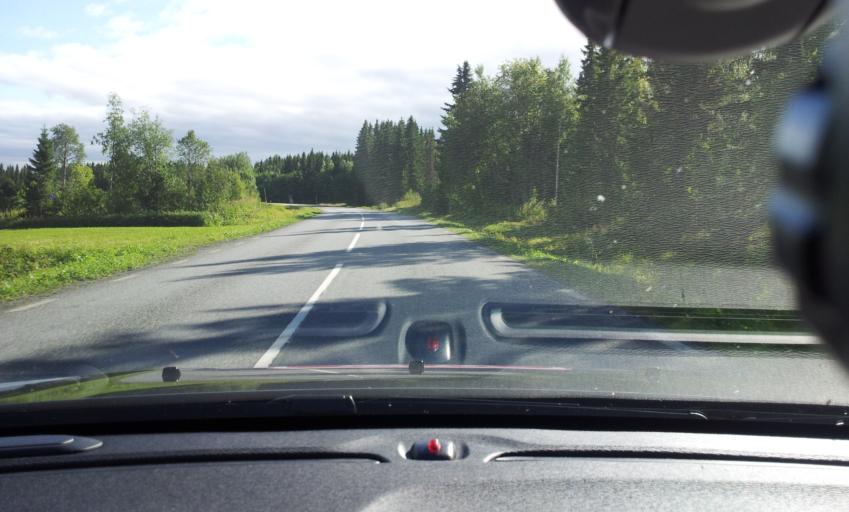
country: SE
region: Jaemtland
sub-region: Krokoms Kommun
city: Krokom
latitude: 63.4804
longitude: 14.1902
